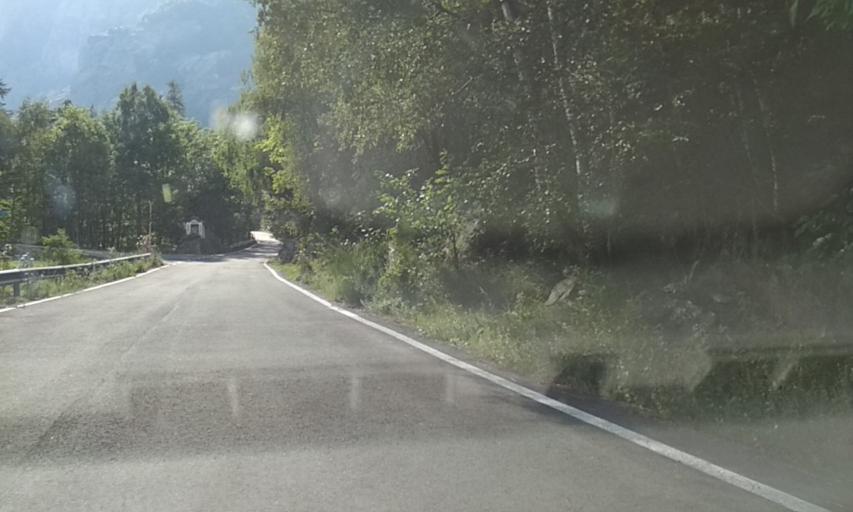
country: IT
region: Piedmont
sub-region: Provincia di Torino
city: Noasca
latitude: 45.4536
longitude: 7.2987
